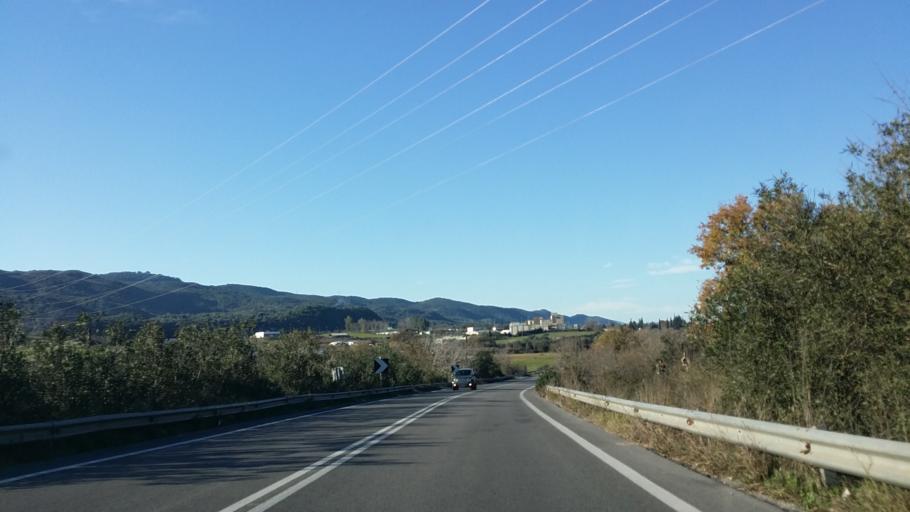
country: GR
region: West Greece
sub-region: Nomos Aitolias kai Akarnanias
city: Fitiai
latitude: 38.6900
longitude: 21.2275
